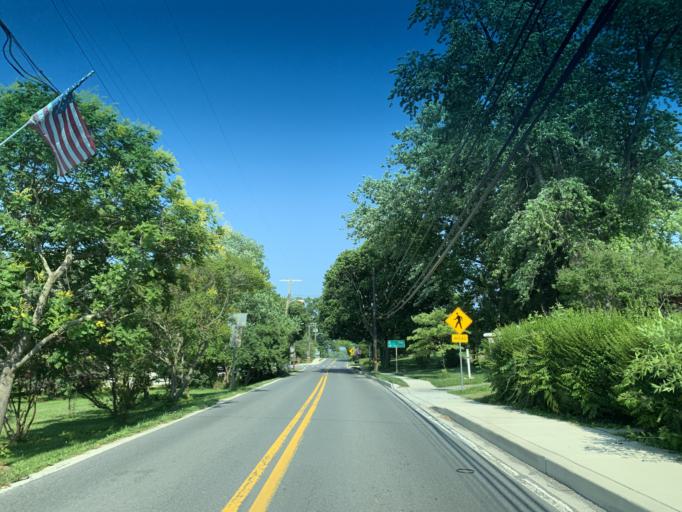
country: US
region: Maryland
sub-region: Montgomery County
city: Poolesville
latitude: 39.2207
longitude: -77.3768
